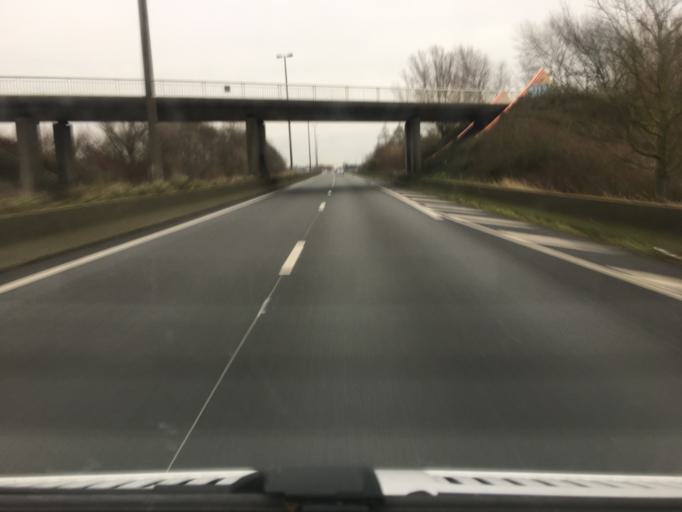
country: FR
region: Nord-Pas-de-Calais
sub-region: Departement du Pas-de-Calais
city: Oye-Plage
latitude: 50.9318
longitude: 2.0188
